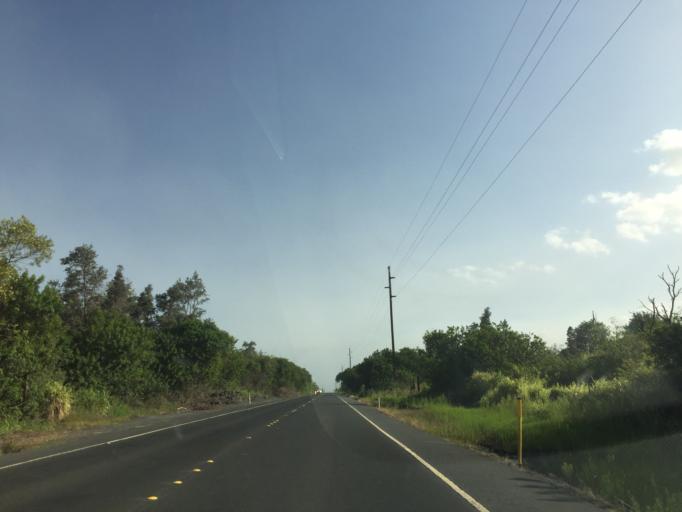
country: US
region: Hawaii
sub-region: Hawaii County
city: Pahala
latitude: 19.2484
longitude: -155.4442
